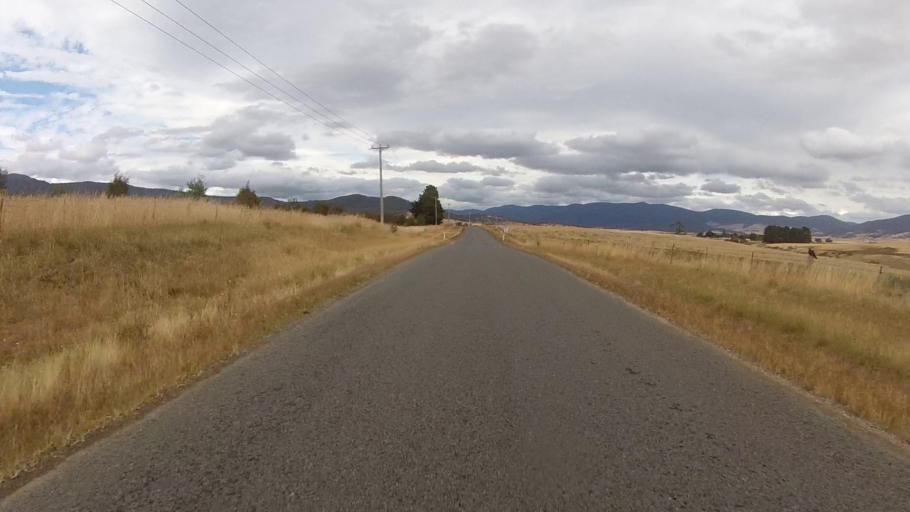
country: AU
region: Tasmania
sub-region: Northern Midlands
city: Evandale
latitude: -41.7852
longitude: 147.7286
